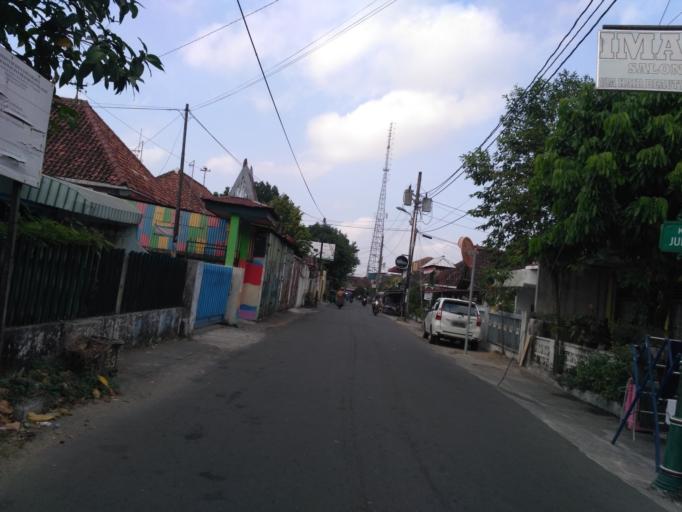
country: ID
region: Daerah Istimewa Yogyakarta
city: Yogyakarta
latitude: -7.7950
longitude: 110.3710
